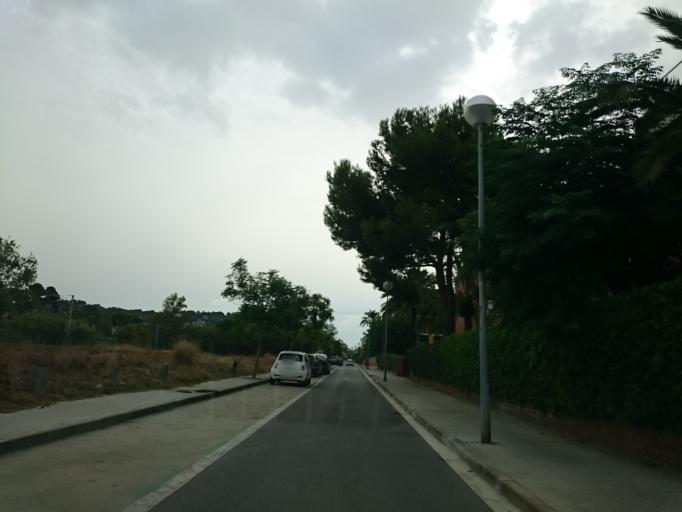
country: ES
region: Catalonia
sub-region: Provincia de Barcelona
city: Castelldefels
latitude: 41.2652
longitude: 1.9445
